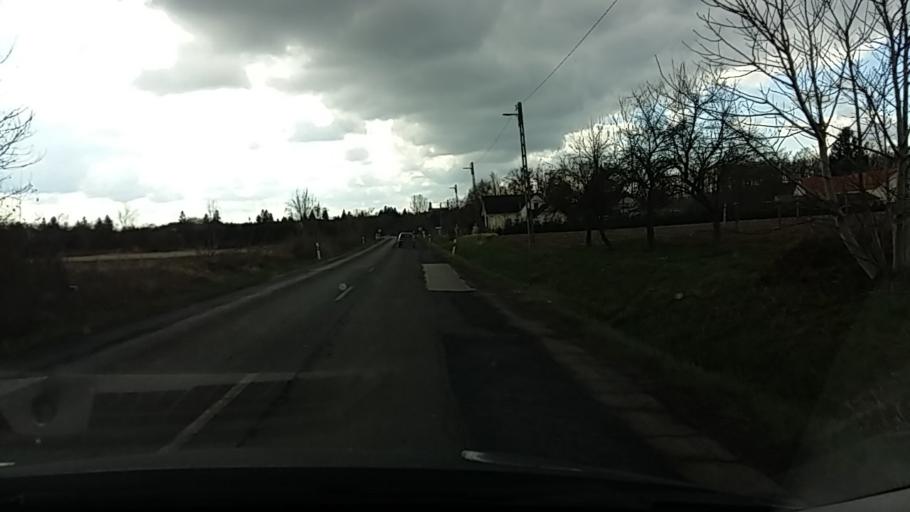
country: HU
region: Somogy
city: Bohonye
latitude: 46.4163
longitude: 17.3830
